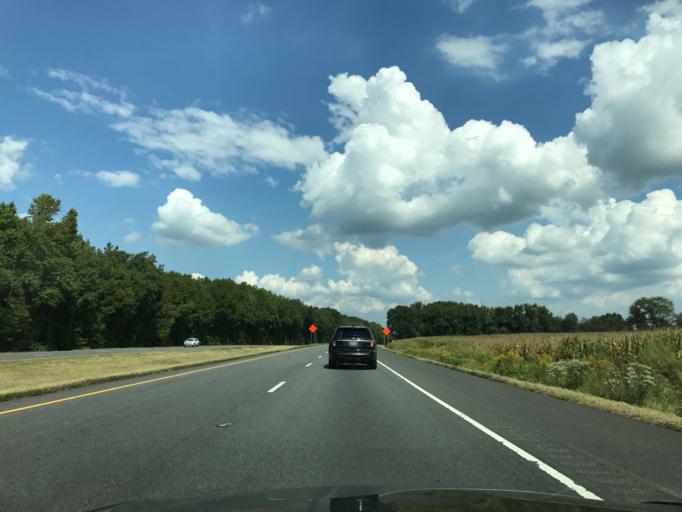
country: US
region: Maryland
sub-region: Queen Anne's County
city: Kingstown
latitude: 39.1922
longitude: -75.9116
